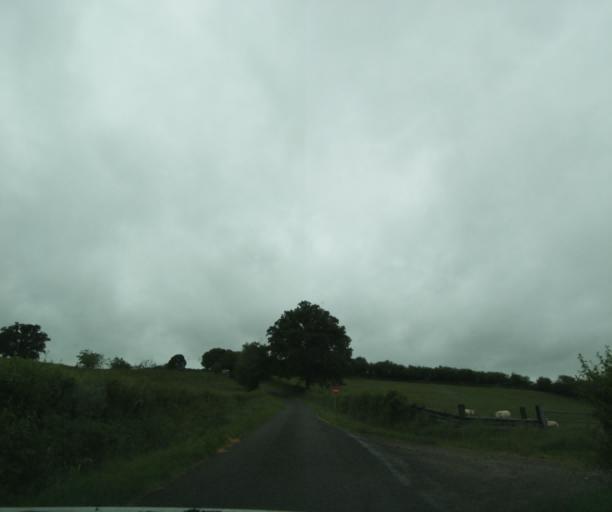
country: FR
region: Bourgogne
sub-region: Departement de Saone-et-Loire
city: Palinges
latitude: 46.5557
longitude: 4.2028
